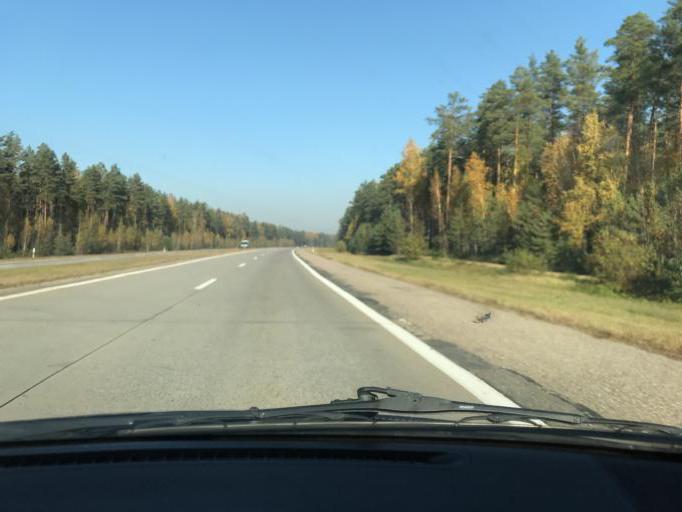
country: BY
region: Minsk
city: Uzda
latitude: 53.4010
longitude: 27.4811
